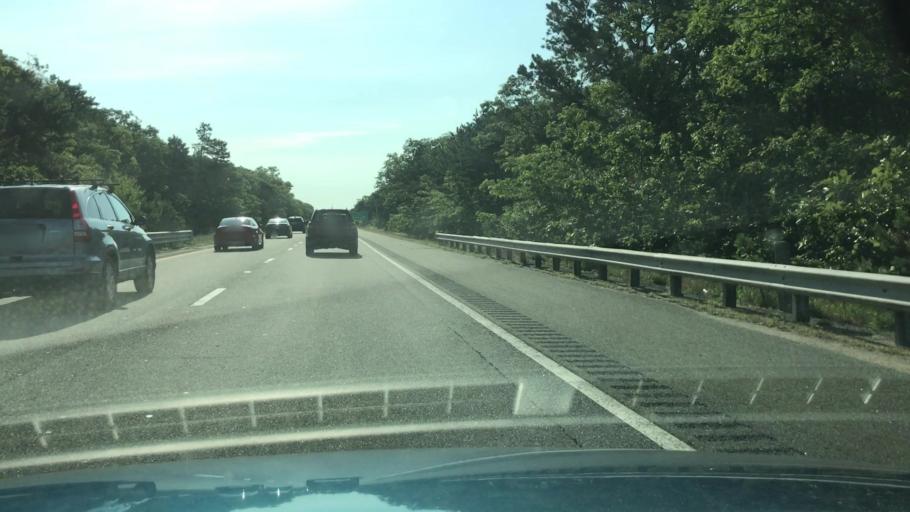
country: US
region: Massachusetts
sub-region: Barnstable County
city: Yarmouth Port
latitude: 41.6874
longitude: -70.2729
